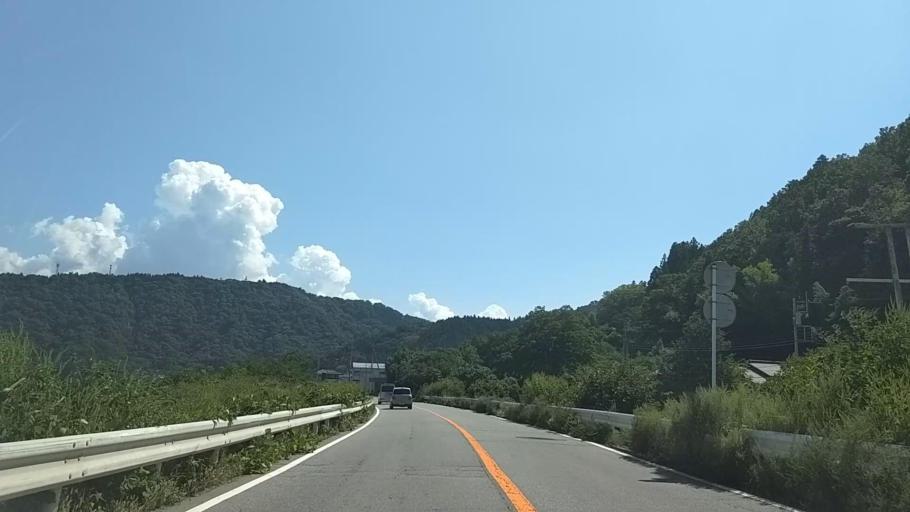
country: JP
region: Yamanashi
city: Ryuo
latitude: 35.5191
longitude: 138.4524
